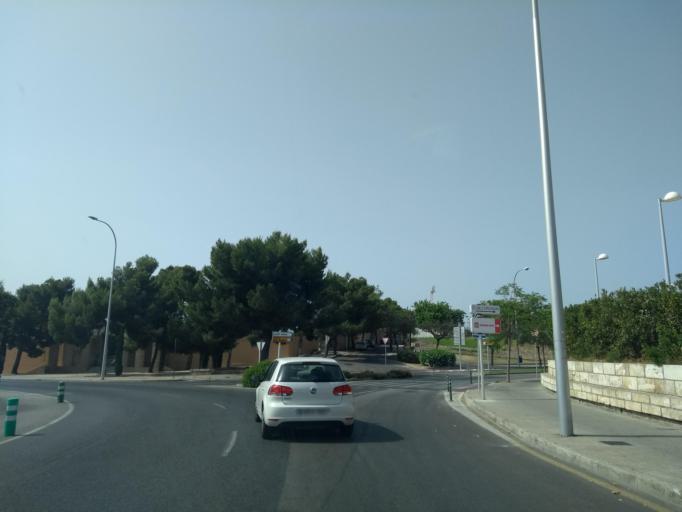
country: ES
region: Balearic Islands
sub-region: Illes Balears
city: Palma
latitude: 39.5854
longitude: 2.6407
